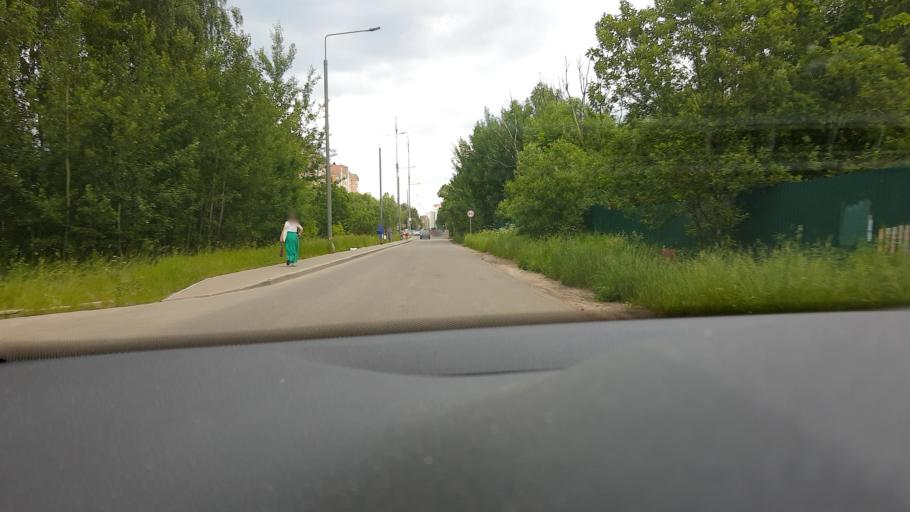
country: RU
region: Moscow
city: Khimki
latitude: 55.8816
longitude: 37.3895
